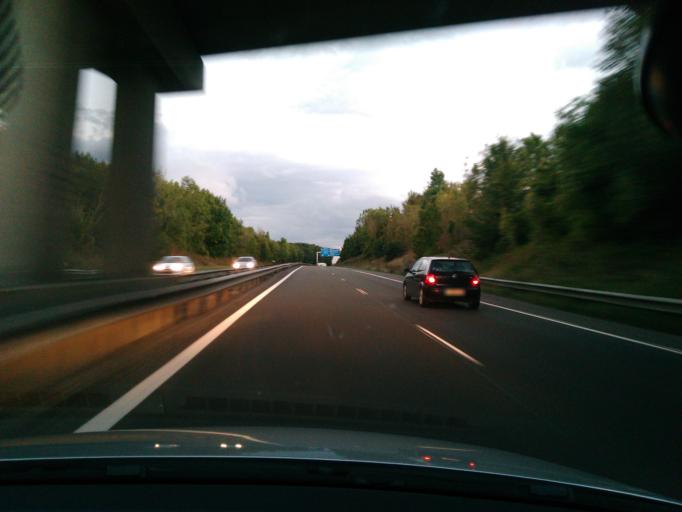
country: FR
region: Ile-de-France
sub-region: Departement de Seine-et-Marne
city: Quincy-Voisins
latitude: 48.8980
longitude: 2.8924
